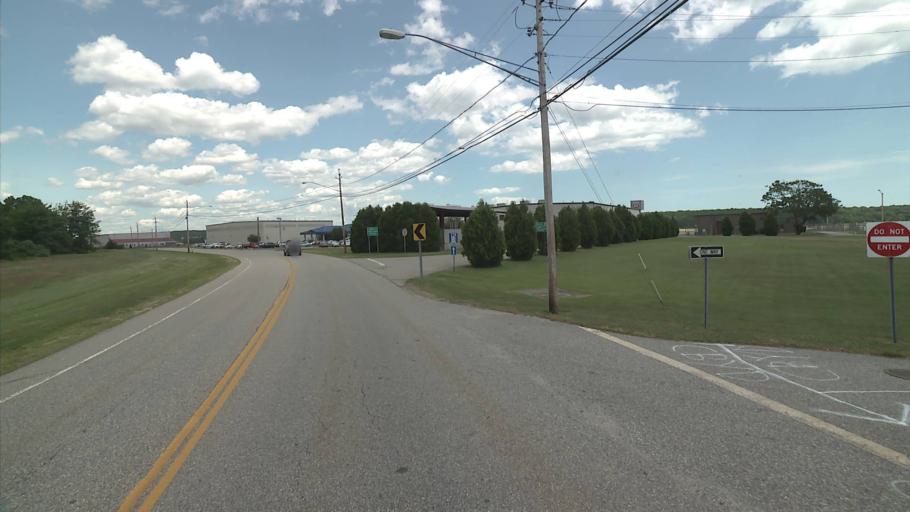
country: US
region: Connecticut
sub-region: New London County
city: Long Hill
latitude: 41.3335
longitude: -72.0459
